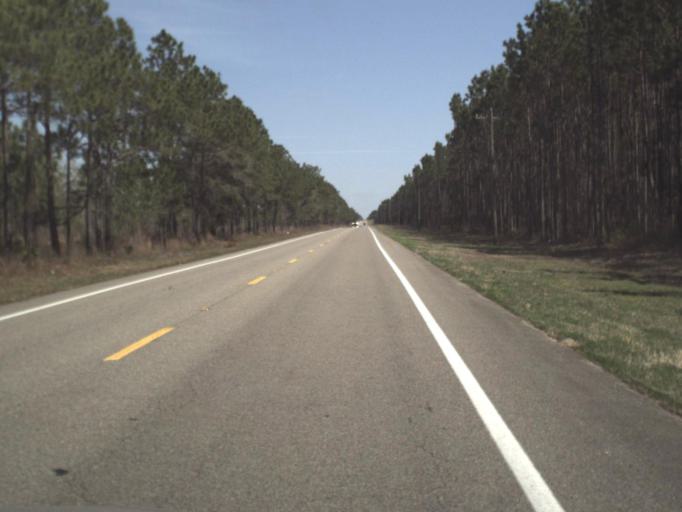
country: US
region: Florida
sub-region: Liberty County
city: Bristol
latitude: 30.4647
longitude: -84.9477
